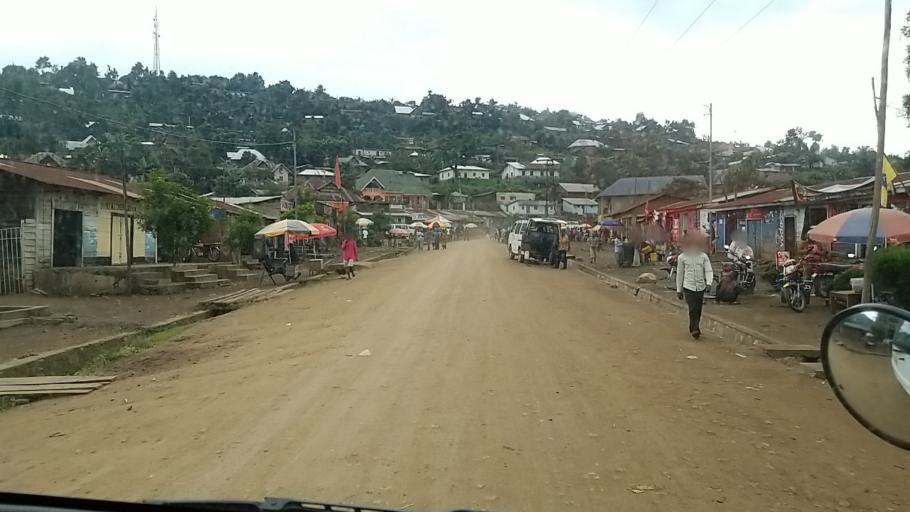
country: CD
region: Nord Kivu
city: Sake
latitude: -1.7085
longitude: 29.0192
